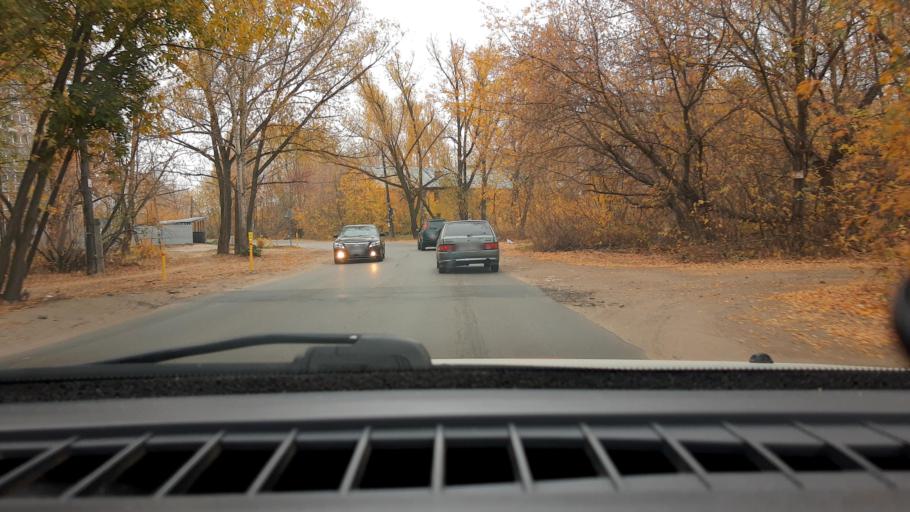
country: RU
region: Nizjnij Novgorod
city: Gorbatovka
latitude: 56.3445
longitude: 43.8302
